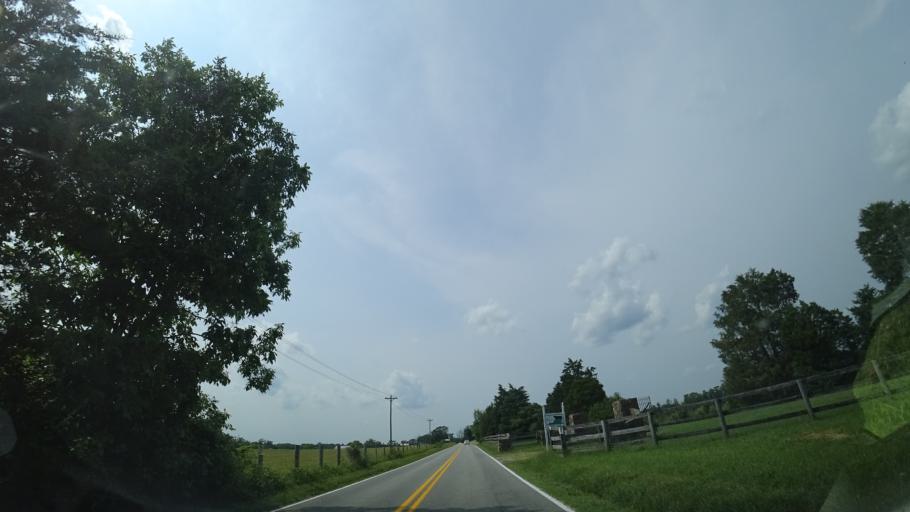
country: US
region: Virginia
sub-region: Spotsylvania County
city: Spotsylvania
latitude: 38.1187
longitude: -77.7676
